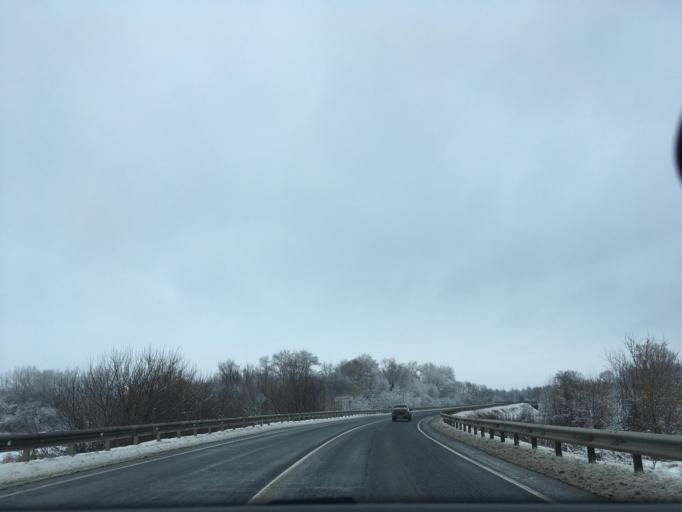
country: RU
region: Voronezj
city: Zabolotovka
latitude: 50.2459
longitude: 39.3747
